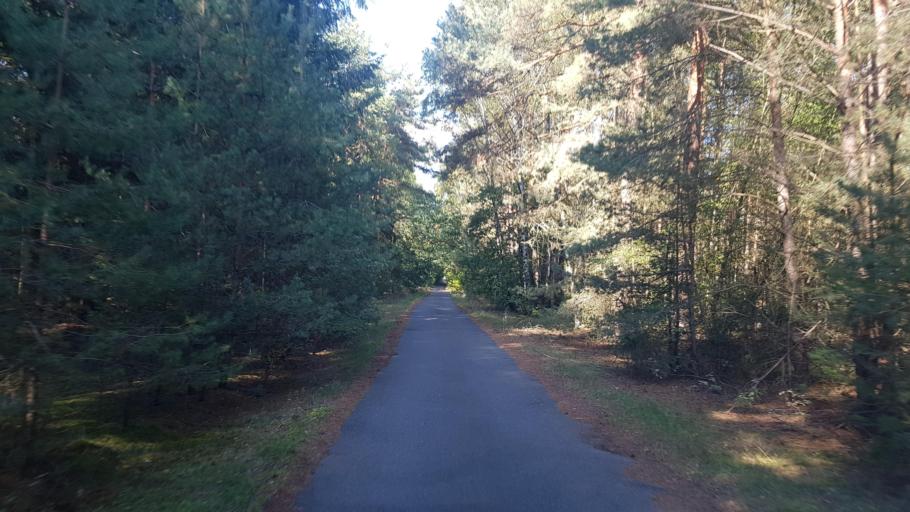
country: DE
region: Brandenburg
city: Ihlow
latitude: 51.8705
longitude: 13.2512
